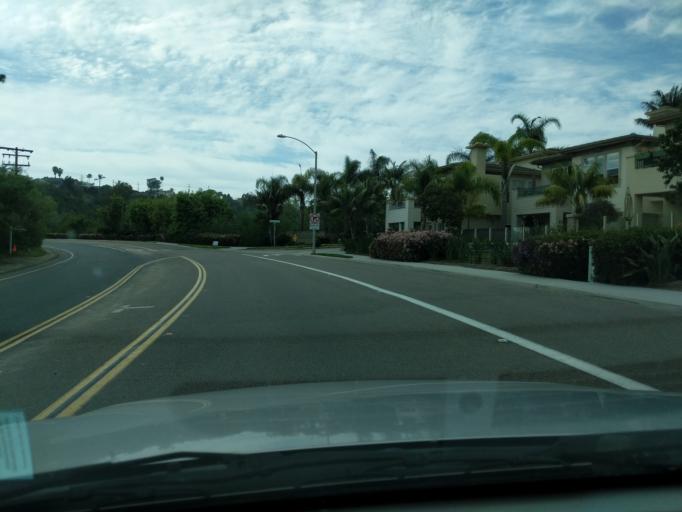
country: US
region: California
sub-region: San Diego County
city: Solana Beach
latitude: 33.0129
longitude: -117.2710
